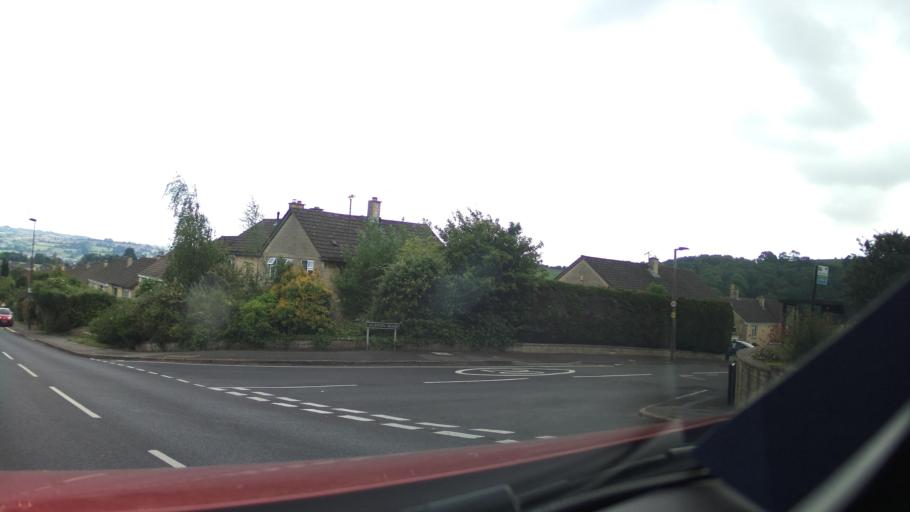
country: GB
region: England
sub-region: Bath and North East Somerset
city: Bath
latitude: 51.4036
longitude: -2.3961
